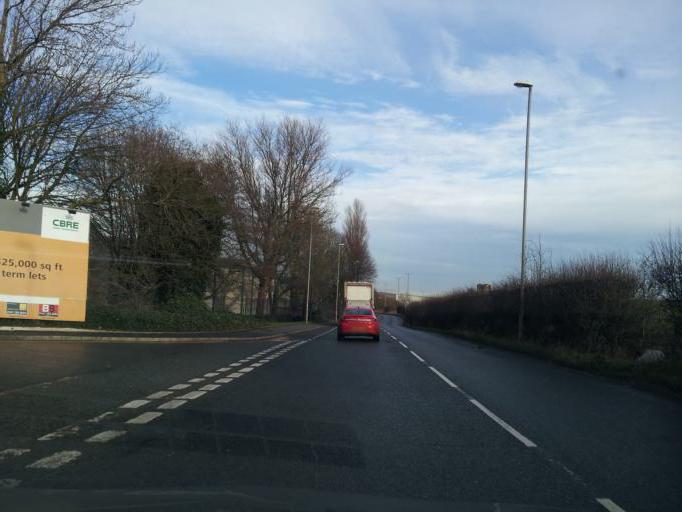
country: GB
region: England
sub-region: Manchester
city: Heywood
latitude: 53.5815
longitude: -2.2380
